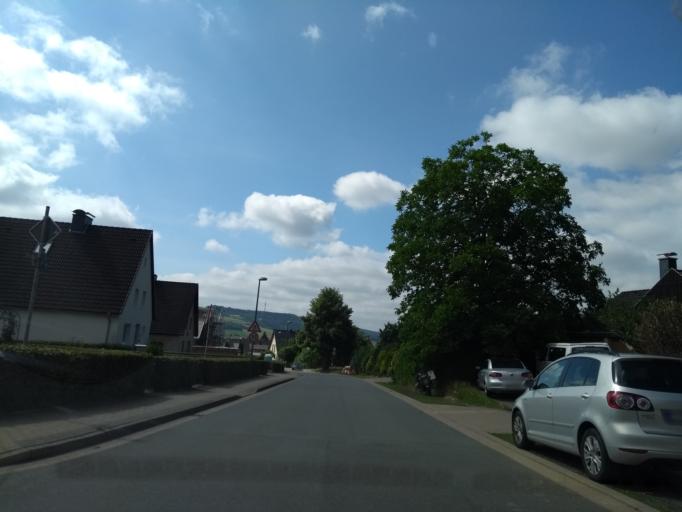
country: DE
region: North Rhine-Westphalia
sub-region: Regierungsbezirk Detmold
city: Lugde
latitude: 51.9598
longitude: 9.2568
